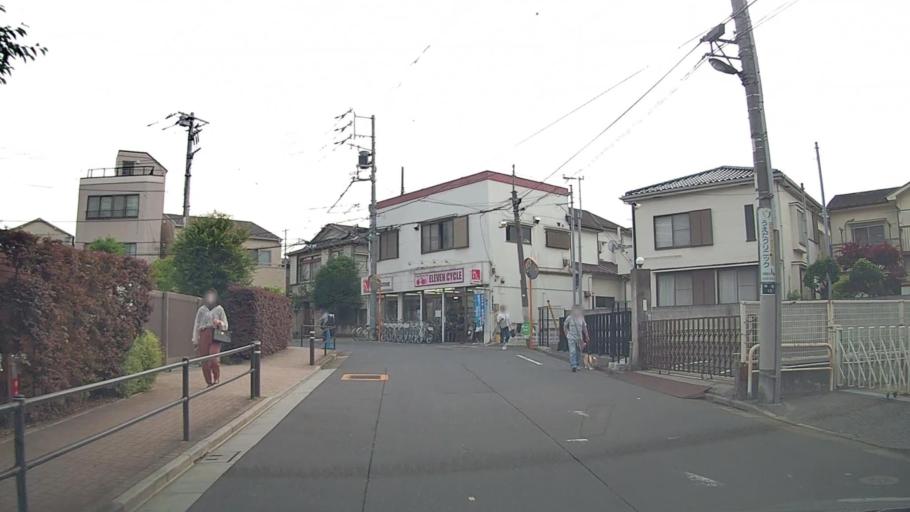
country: JP
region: Saitama
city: Kawaguchi
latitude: 35.7588
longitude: 139.7122
